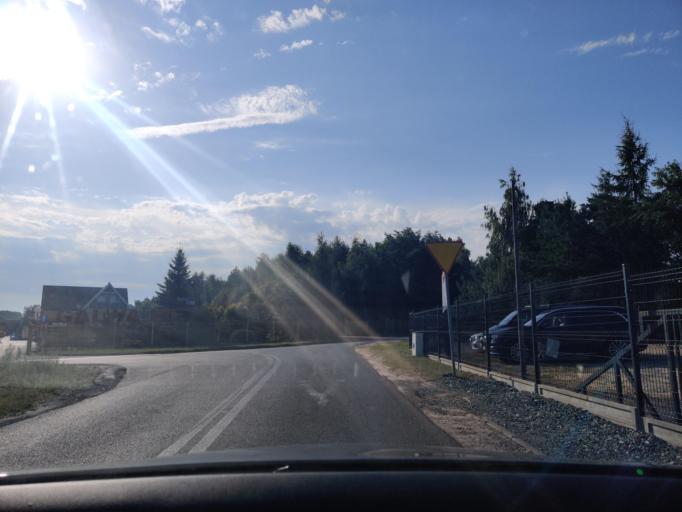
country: PL
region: Greater Poland Voivodeship
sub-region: Konin
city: Konin
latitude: 52.1842
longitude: 18.3311
